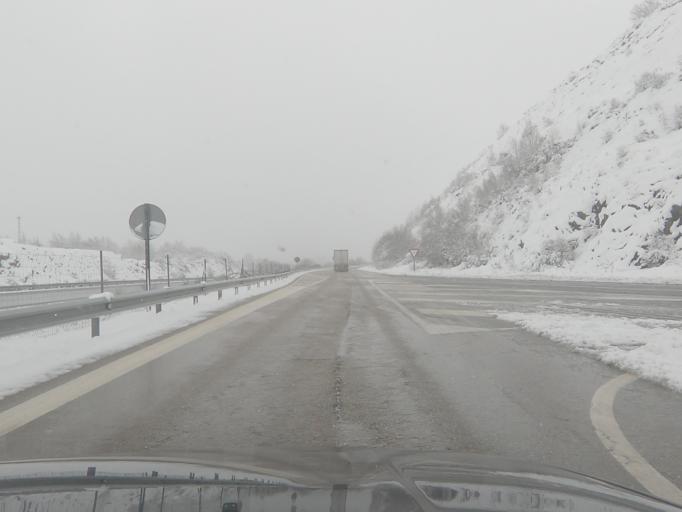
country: ES
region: Castille and Leon
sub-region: Provincia de Zamora
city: Lubian
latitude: 42.0345
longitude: -6.8696
